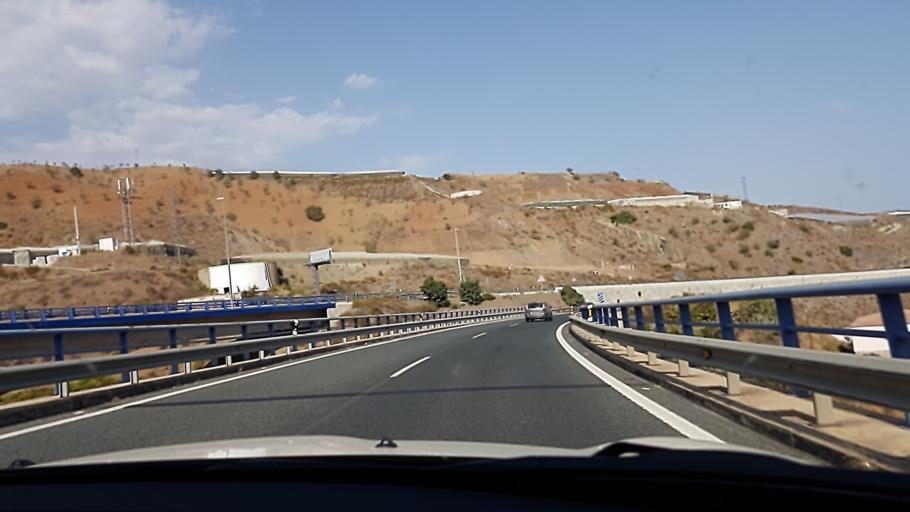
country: ES
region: Andalusia
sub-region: Provincia de Granada
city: Polopos
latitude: 36.7510
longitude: -3.3220
